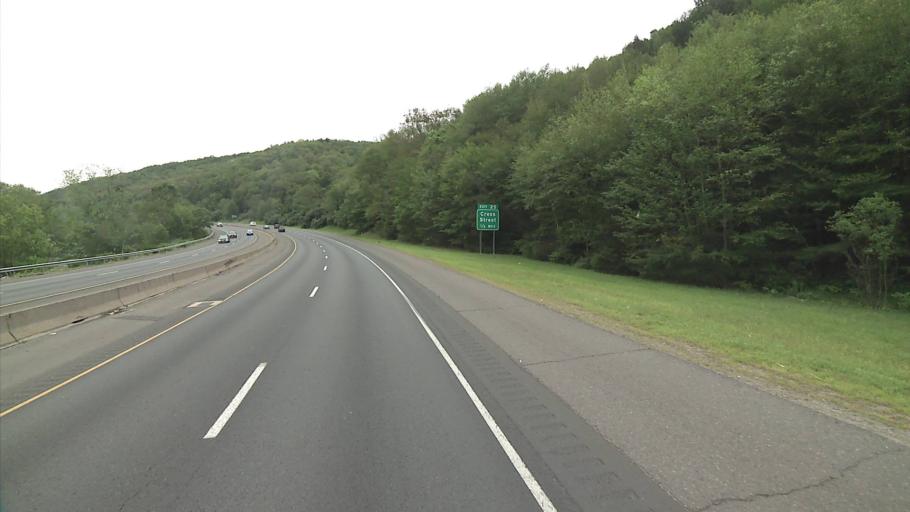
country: US
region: Connecticut
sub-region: New Haven County
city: Naugatuck
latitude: 41.4595
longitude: -73.0555
